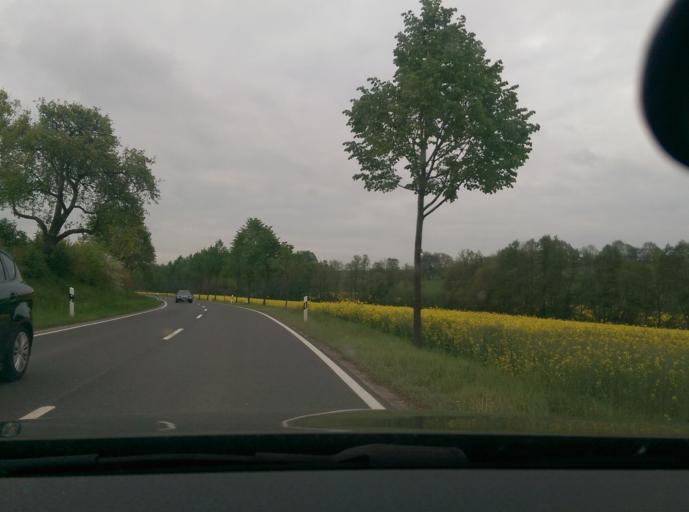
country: DE
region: Thuringia
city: Creuzburg
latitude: 51.0337
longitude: 10.2521
